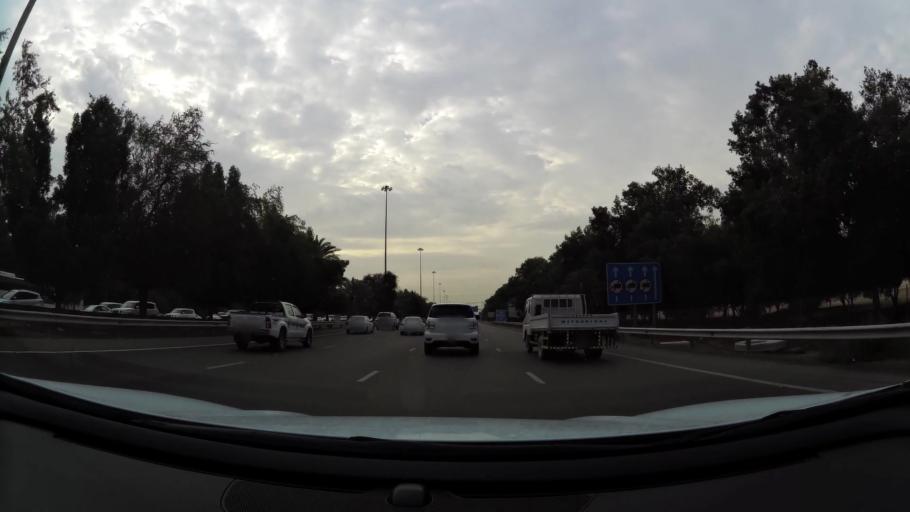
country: AE
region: Abu Dhabi
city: Abu Dhabi
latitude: 24.3370
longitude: 54.5789
